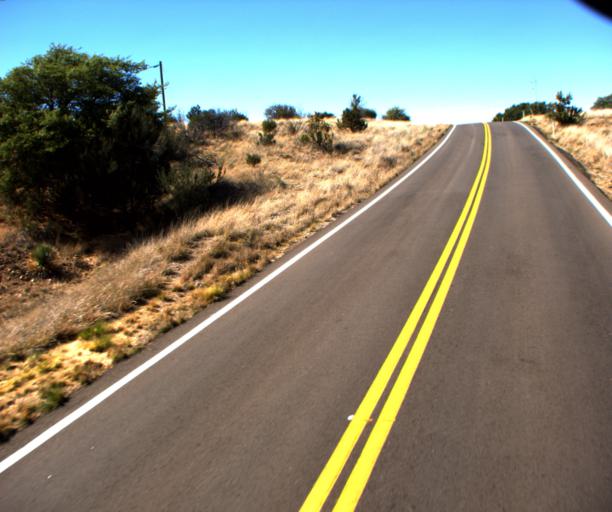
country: US
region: Arizona
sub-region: Cochise County
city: Huachuca City
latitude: 31.5612
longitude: -110.5543
